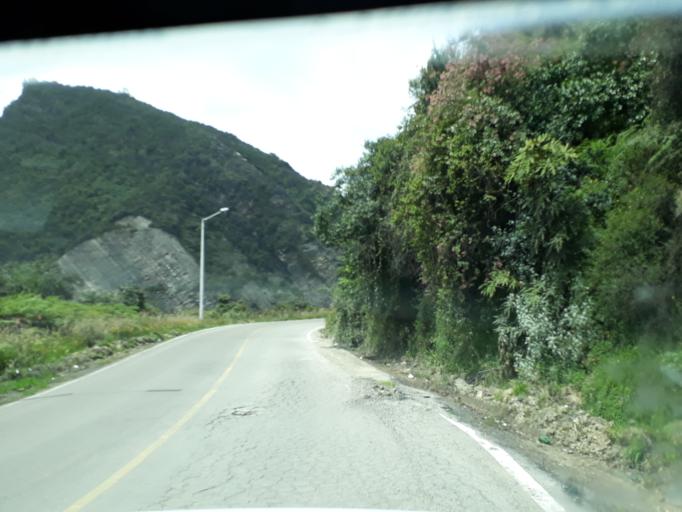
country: CO
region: Cundinamarca
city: Sutatausa
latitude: 5.1899
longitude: -73.8844
